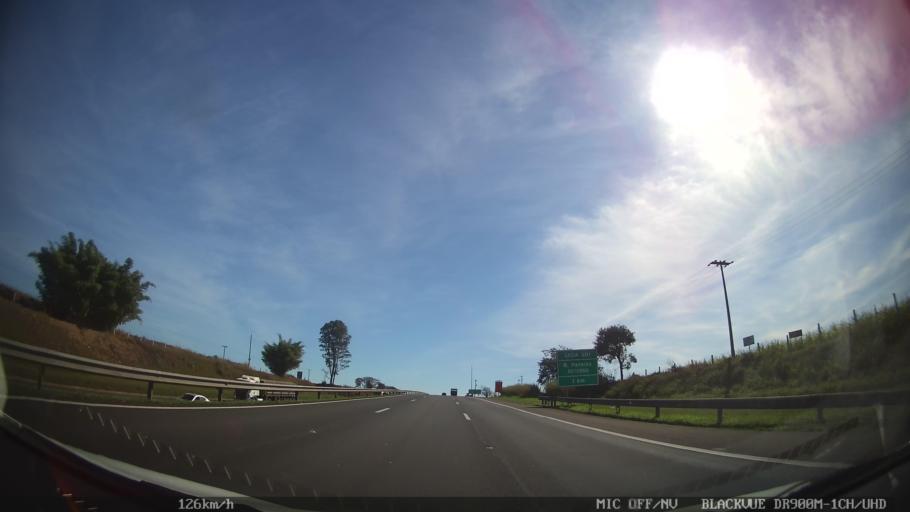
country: BR
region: Sao Paulo
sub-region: Pirassununga
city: Pirassununga
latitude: -22.0869
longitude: -47.4197
